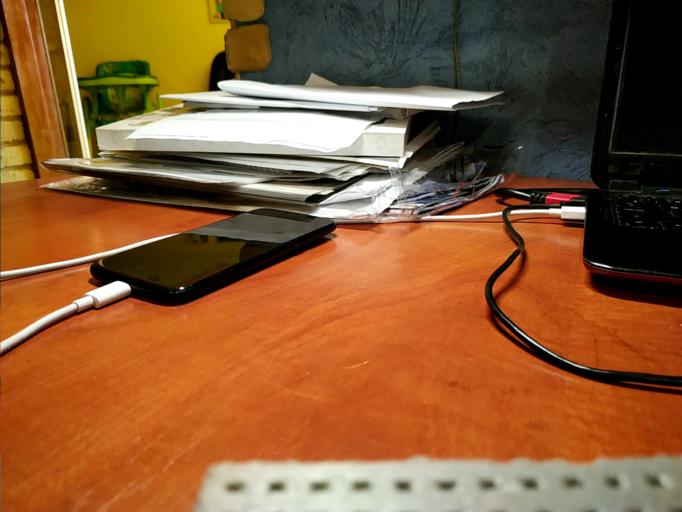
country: RU
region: Tverskaya
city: Kalashnikovo
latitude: 57.3969
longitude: 35.2523
